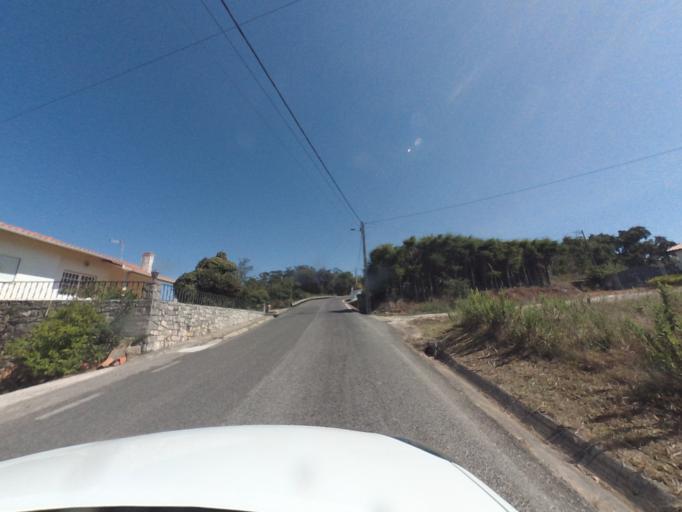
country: PT
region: Leiria
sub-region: Alcobaca
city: Turquel
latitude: 39.4848
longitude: -8.9895
